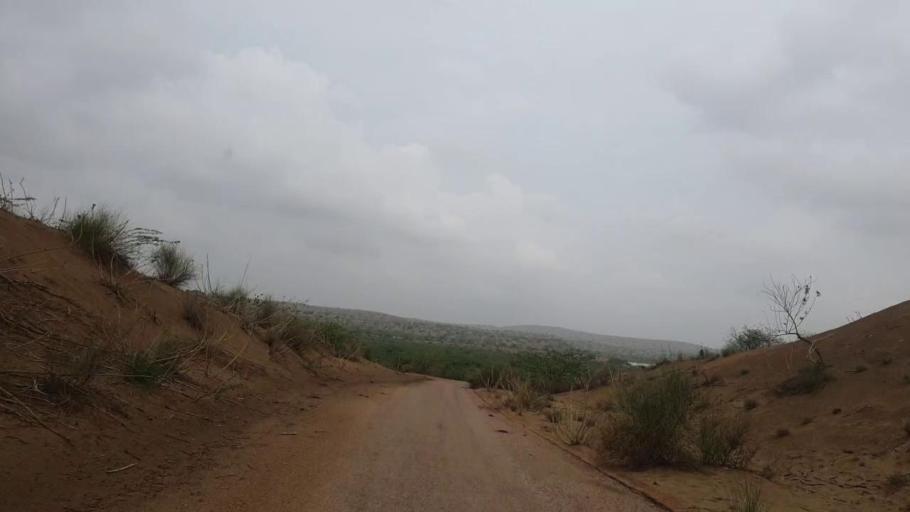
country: PK
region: Sindh
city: Diplo
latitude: 24.5149
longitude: 69.4743
